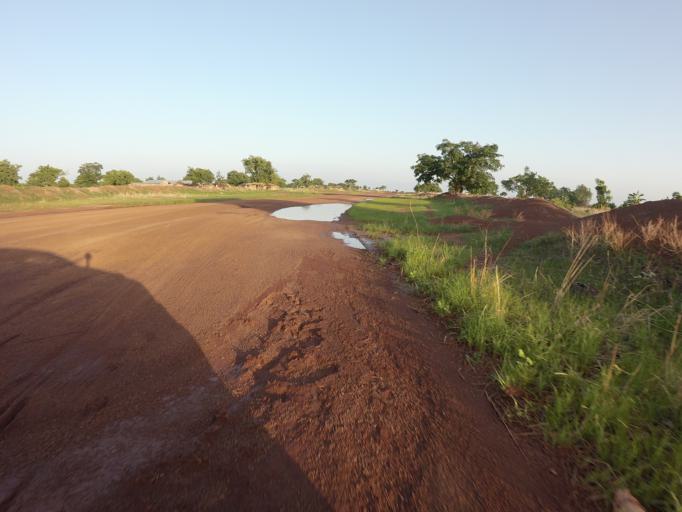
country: TG
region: Savanes
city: Sansanne-Mango
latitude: 10.2317
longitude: -0.0726
